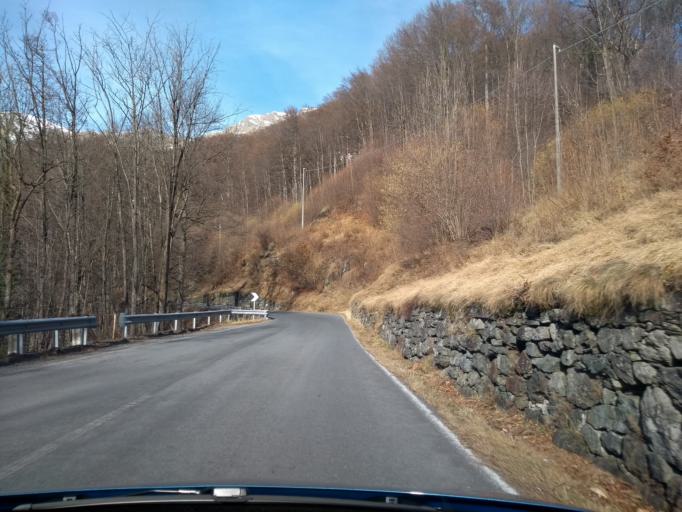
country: IT
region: Piedmont
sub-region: Provincia di Torino
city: Ala di Stura
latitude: 45.3129
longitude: 7.3160
